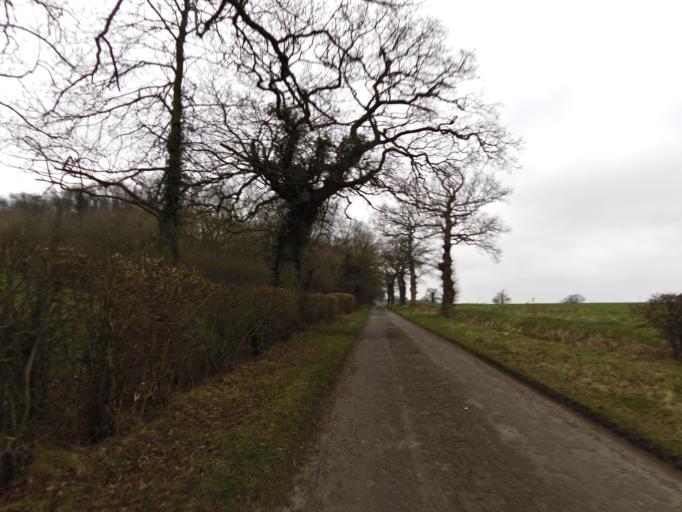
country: GB
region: England
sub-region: Suffolk
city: Framlingham
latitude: 52.2379
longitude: 1.3894
